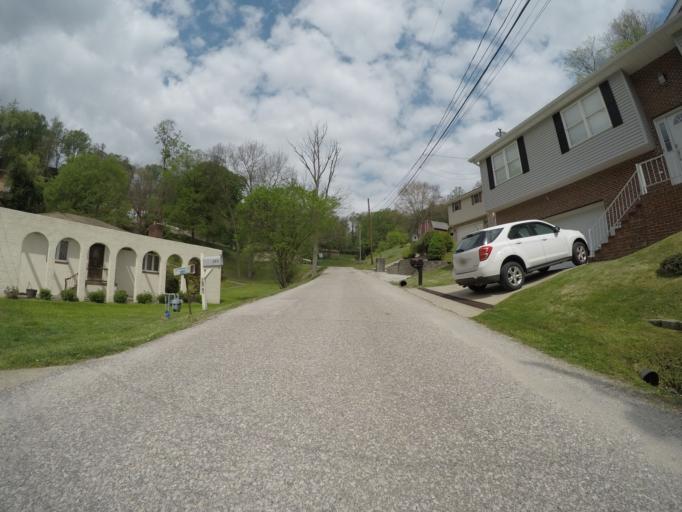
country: US
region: West Virginia
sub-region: Kanawha County
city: Charleston
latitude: 38.3840
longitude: -81.6057
